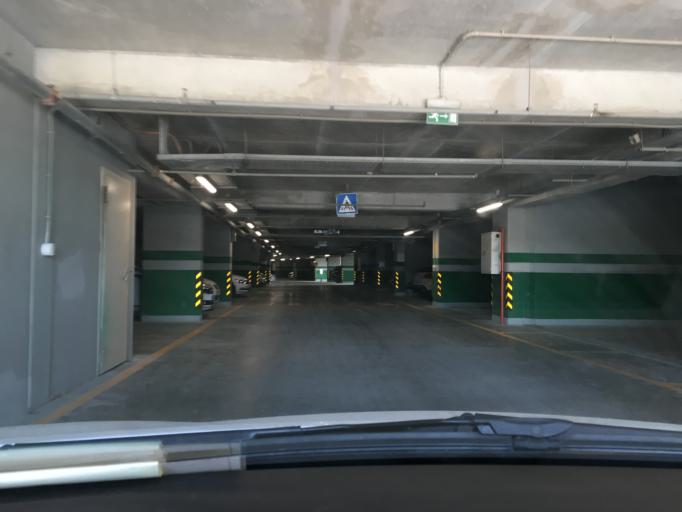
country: TR
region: Istanbul
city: Sisli
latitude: 41.0908
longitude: 28.9464
